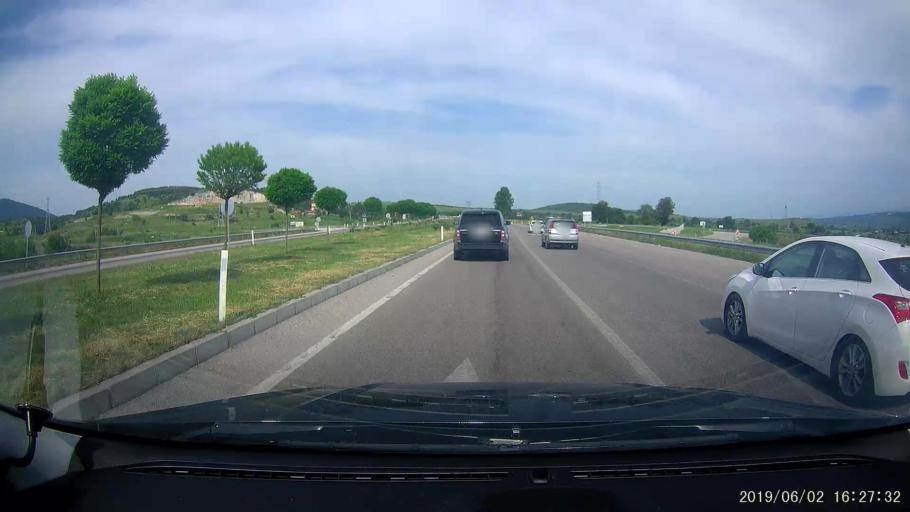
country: TR
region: Samsun
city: Ladik
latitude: 41.0021
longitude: 35.8295
